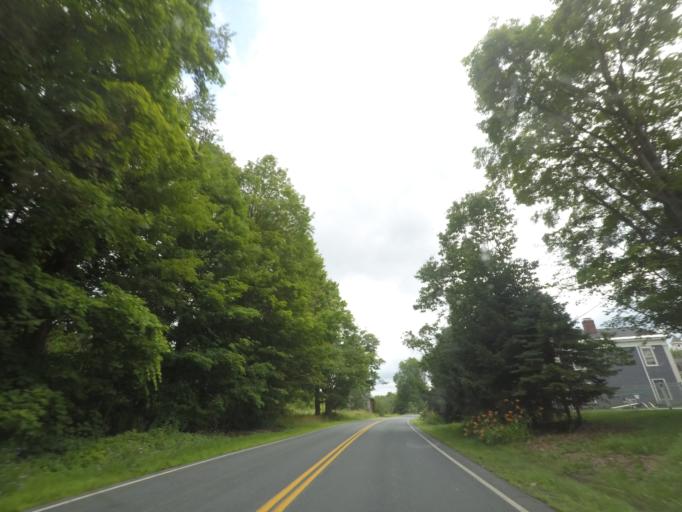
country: US
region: New York
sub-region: Saratoga County
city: Stillwater
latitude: 42.8787
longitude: -73.5594
